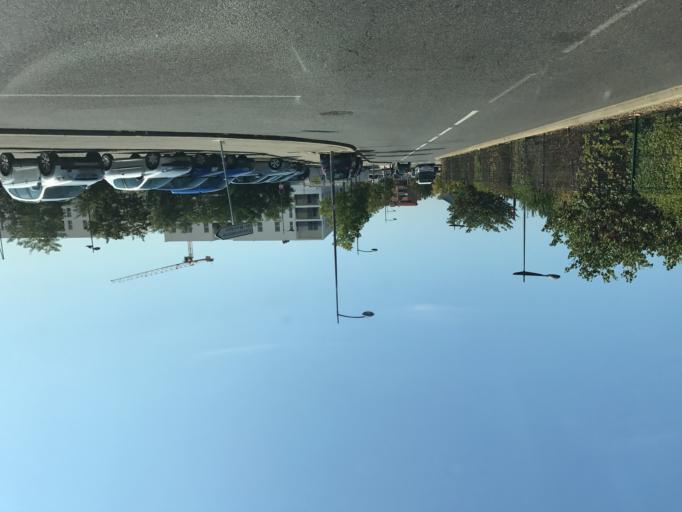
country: FR
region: Rhone-Alpes
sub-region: Departement du Rhone
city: Meyzieu
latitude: 45.7716
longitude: 4.9974
